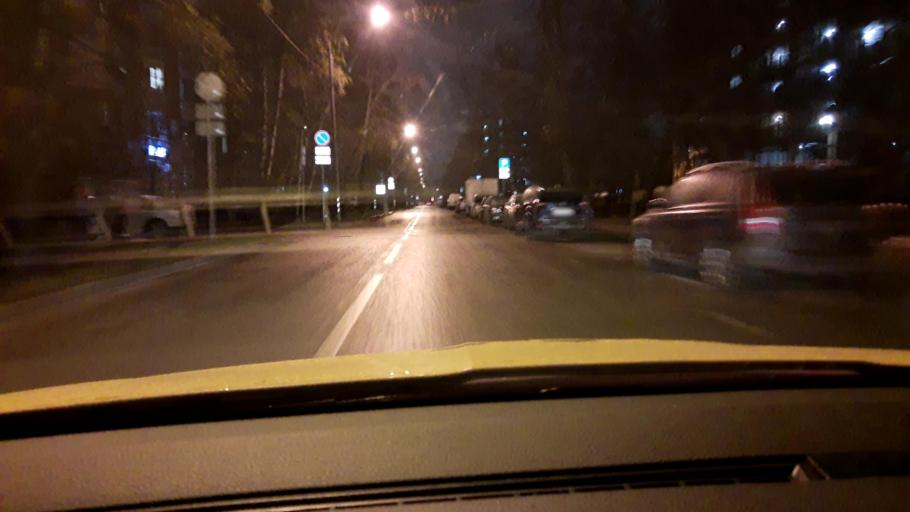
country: RU
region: Moscow
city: Kozeyevo
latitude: 55.8927
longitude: 37.6471
